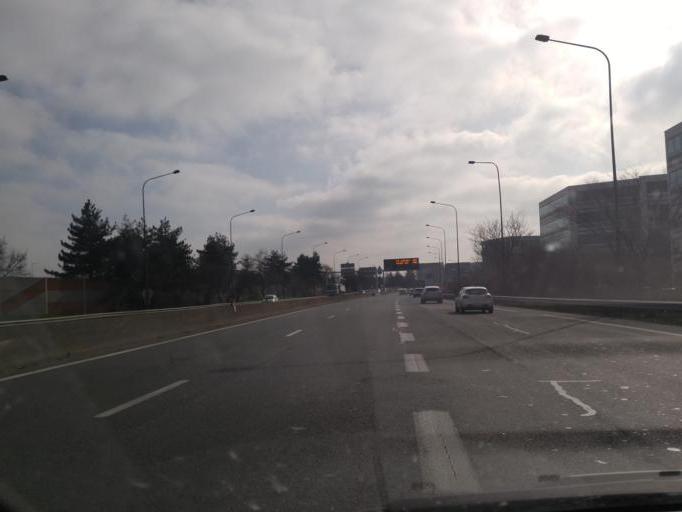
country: FR
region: Midi-Pyrenees
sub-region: Departement de la Haute-Garonne
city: Blagnac
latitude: 43.6303
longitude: 1.3823
